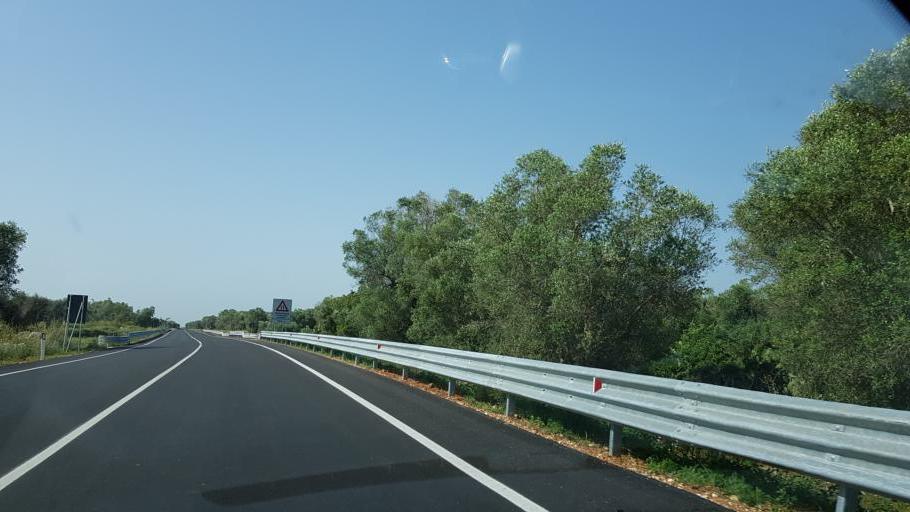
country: IT
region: Apulia
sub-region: Provincia di Brindisi
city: San Pancrazio Salentino
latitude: 40.4660
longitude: 17.8384
